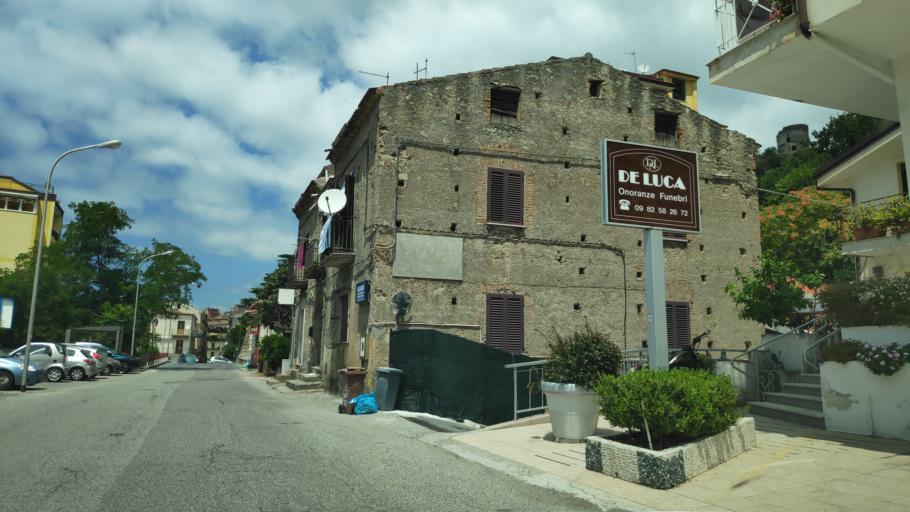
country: IT
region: Calabria
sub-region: Provincia di Cosenza
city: Paola
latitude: 39.3568
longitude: 16.0429
